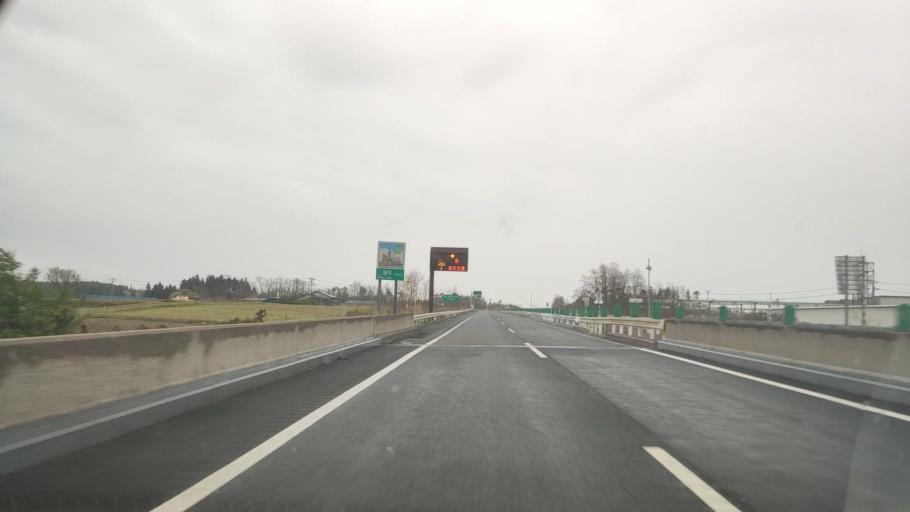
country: JP
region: Akita
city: Noshiromachi
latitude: 40.1247
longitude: 140.0123
